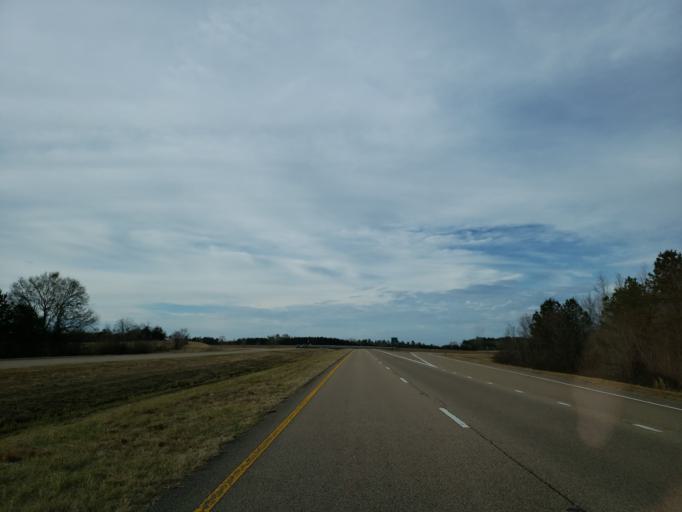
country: US
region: Mississippi
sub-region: Wayne County
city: Waynesboro
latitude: 31.6771
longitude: -88.6113
